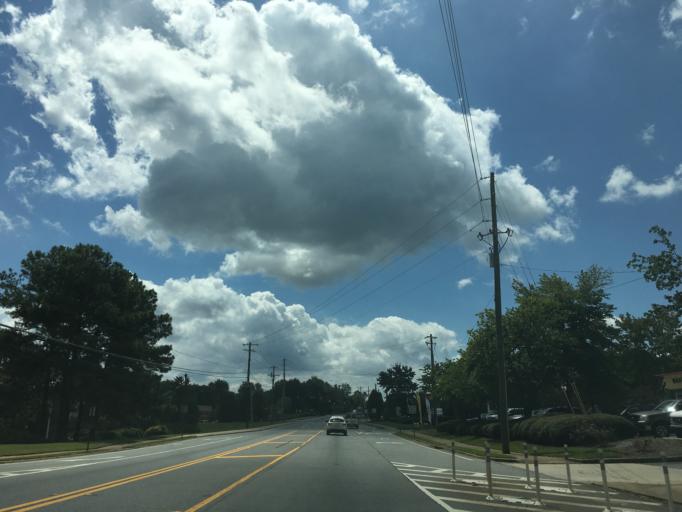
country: US
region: Georgia
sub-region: Fulton County
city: Roswell
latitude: 34.0836
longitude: -84.3582
